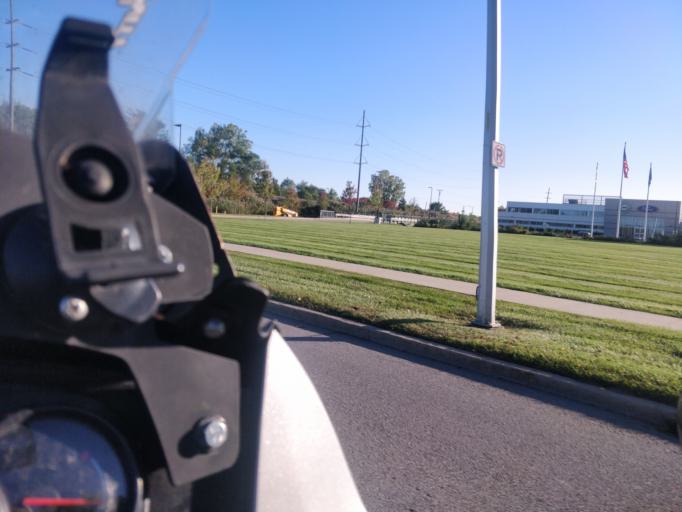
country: US
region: Michigan
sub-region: Wayne County
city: Melvindale
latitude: 42.2671
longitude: -83.1772
